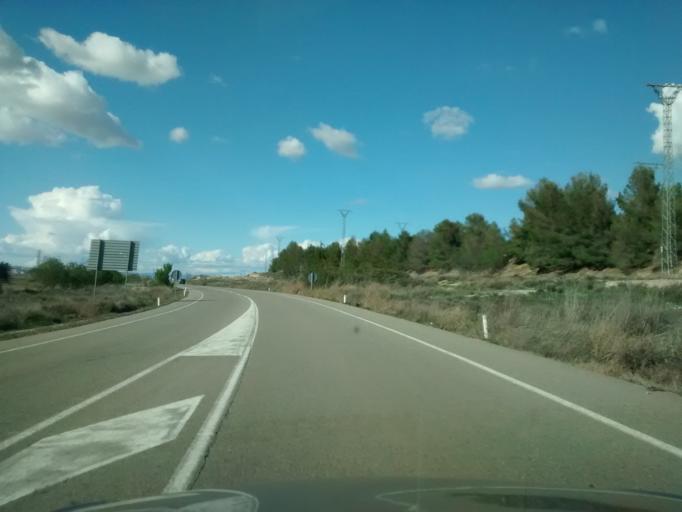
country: ES
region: Aragon
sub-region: Provincia de Zaragoza
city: San Mateo de Gallego
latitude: 41.8123
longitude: -0.7751
